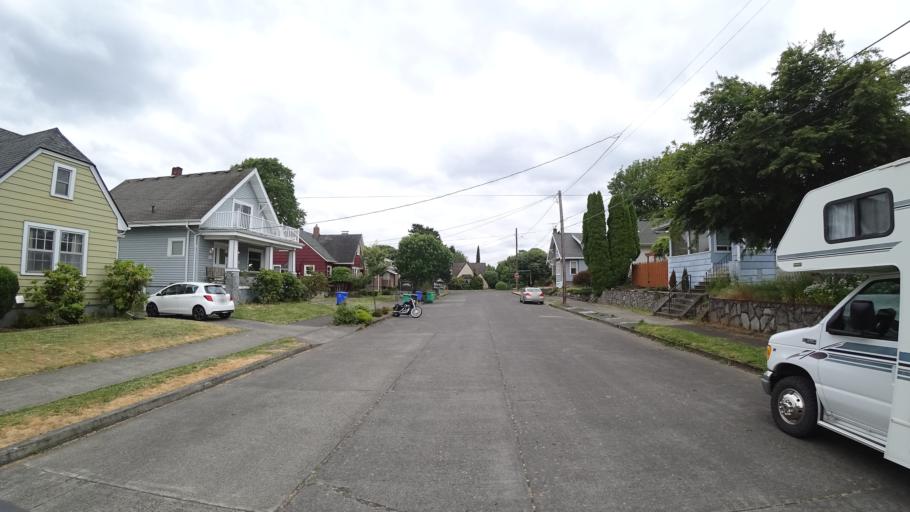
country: US
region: Oregon
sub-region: Multnomah County
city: Portland
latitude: 45.4928
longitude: -122.6552
